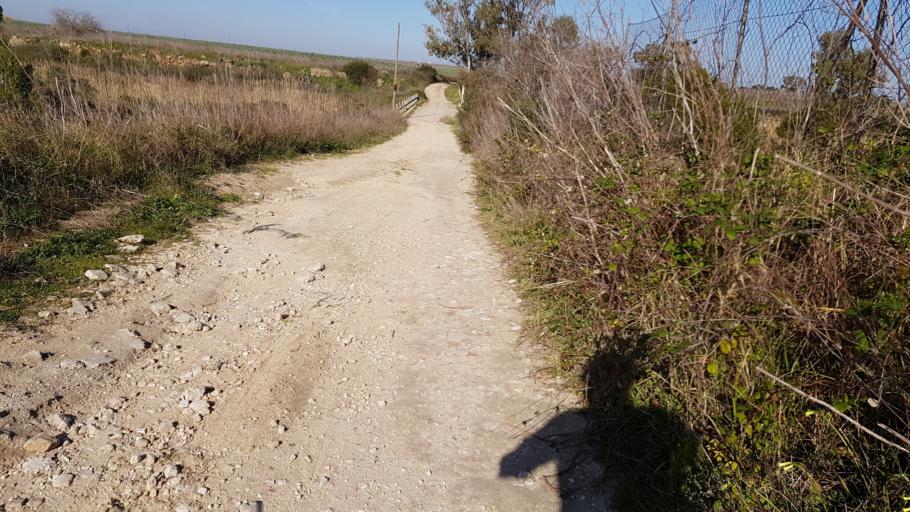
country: IT
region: Apulia
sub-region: Provincia di Brindisi
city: Brindisi
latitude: 40.6246
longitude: 17.8948
